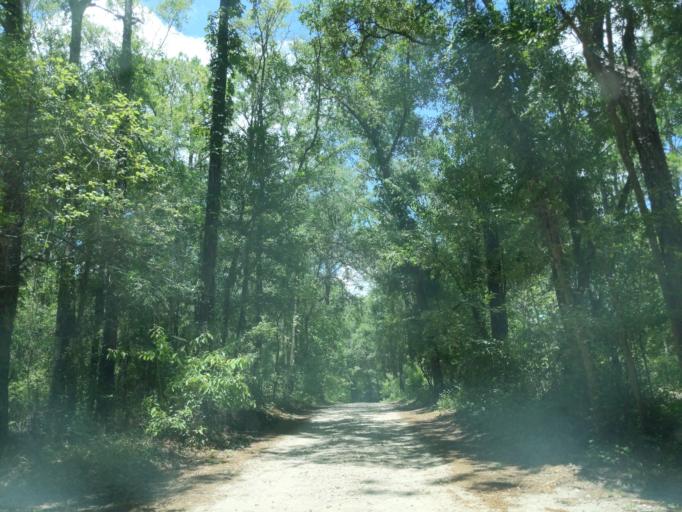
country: US
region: Florida
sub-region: Leon County
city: Tallahassee
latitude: 30.4035
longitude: -84.3445
